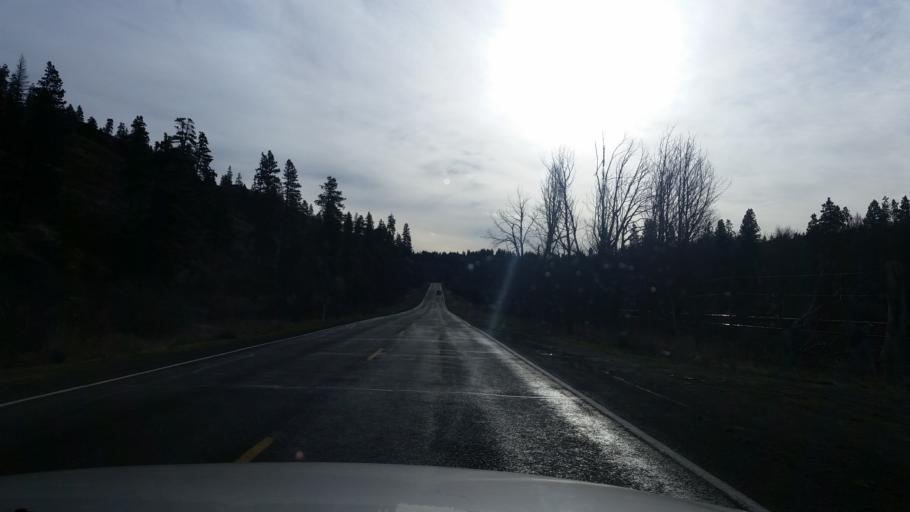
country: US
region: Washington
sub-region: Kittitas County
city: Cle Elum
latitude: 47.1409
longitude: -120.7940
